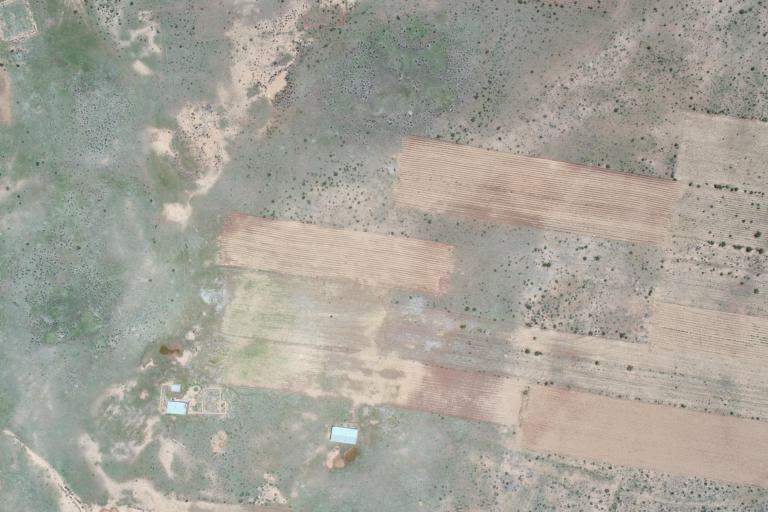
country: BO
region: La Paz
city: Patacamaya
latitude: -17.2755
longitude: -68.5125
